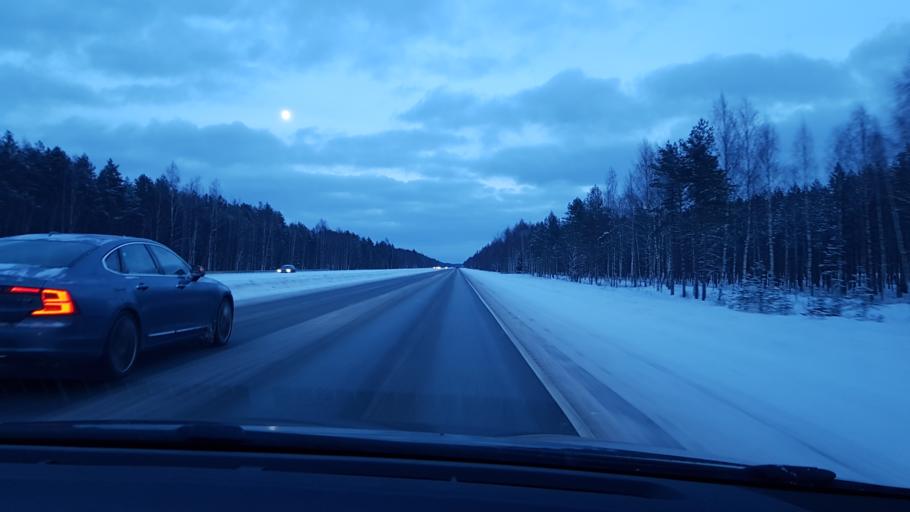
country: EE
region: Harju
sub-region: Kuusalu vald
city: Kuusalu
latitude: 59.4585
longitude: 25.5587
